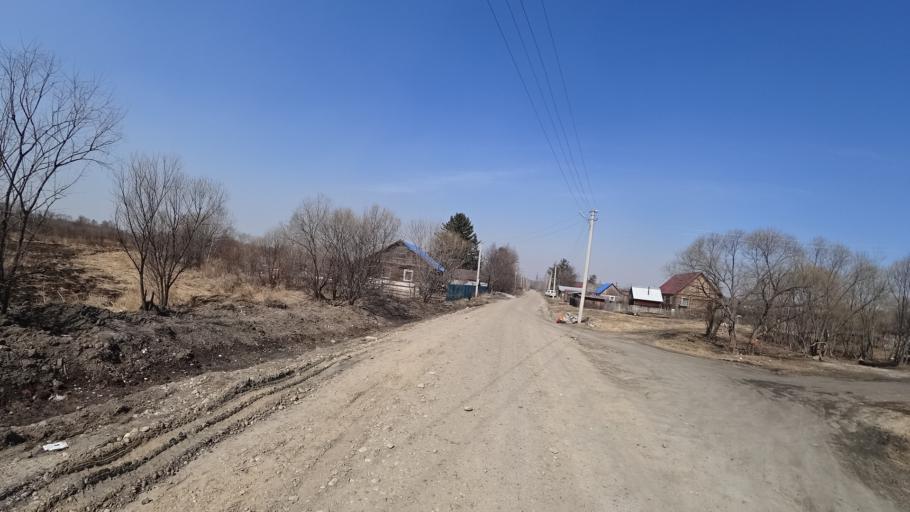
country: RU
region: Amur
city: Novobureyskiy
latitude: 49.7882
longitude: 129.8545
